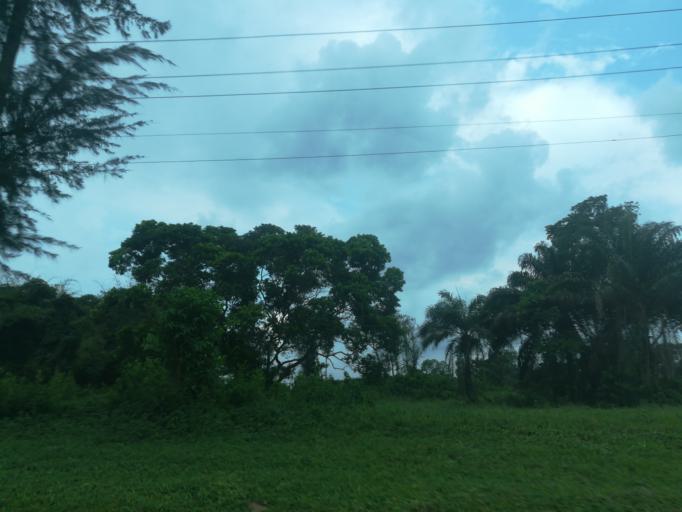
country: NG
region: Lagos
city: Ikorodu
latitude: 6.6356
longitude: 3.5226
